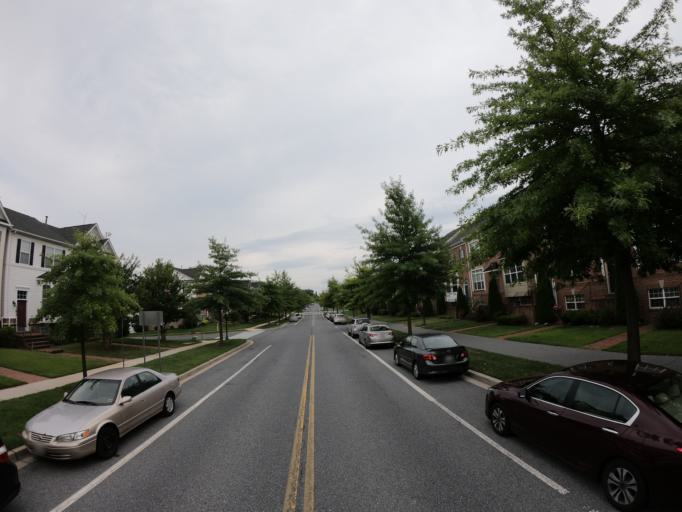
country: US
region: Maryland
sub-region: Montgomery County
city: Clarksburg
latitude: 39.2340
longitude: -77.2441
